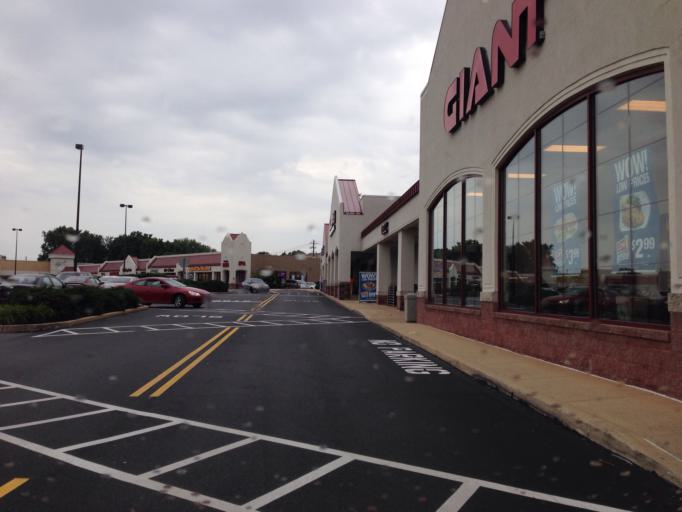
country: US
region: Pennsylvania
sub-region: Lancaster County
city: East Petersburg
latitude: 40.0755
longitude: -76.3255
